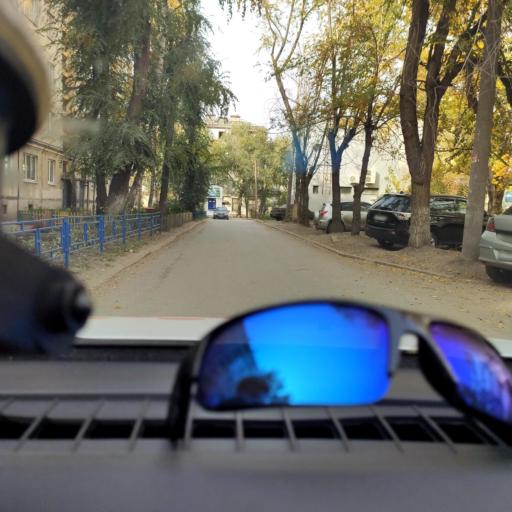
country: RU
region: Samara
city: Samara
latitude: 53.1214
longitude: 50.0905
